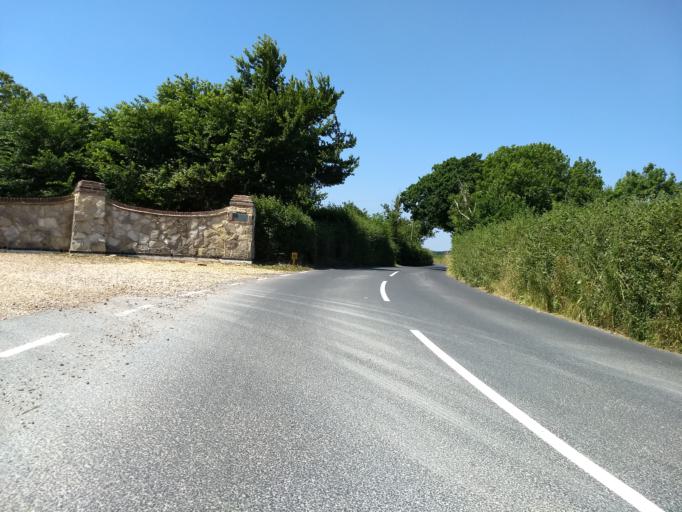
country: GB
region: England
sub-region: Isle of Wight
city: Northwood
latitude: 50.7092
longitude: -1.3566
